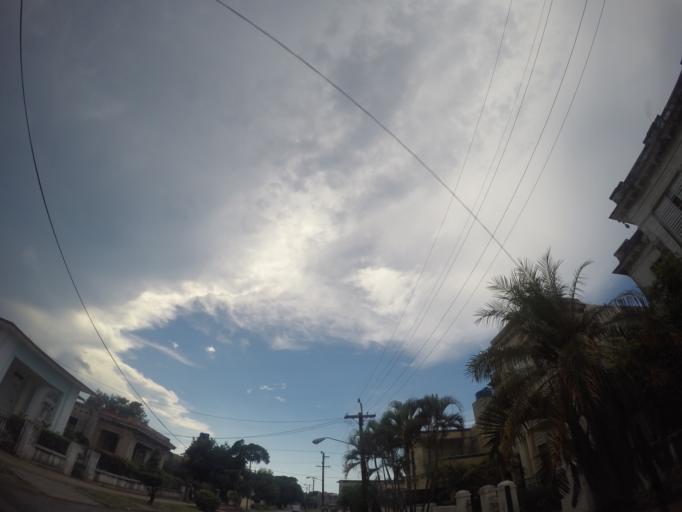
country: CU
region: La Habana
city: Havana
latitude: 23.1161
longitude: -82.4194
